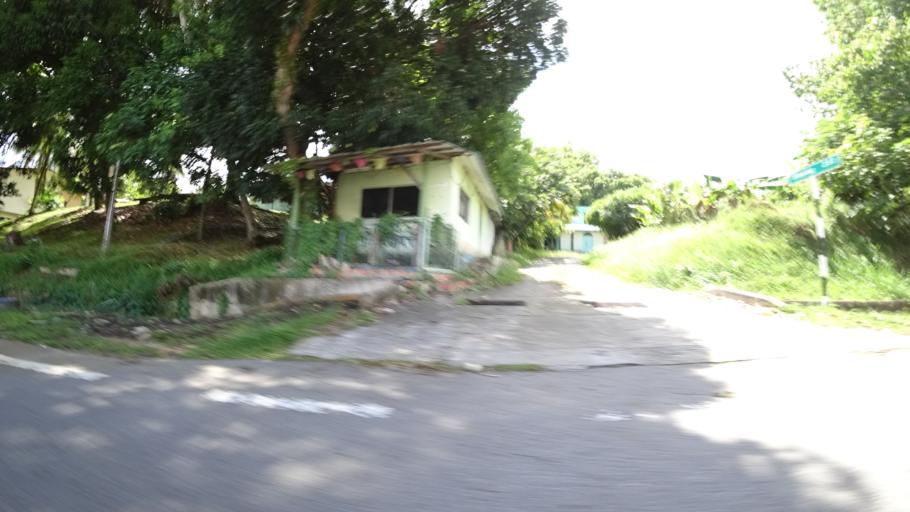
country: BN
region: Brunei and Muara
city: Bandar Seri Begawan
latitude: 4.8753
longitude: 114.9570
